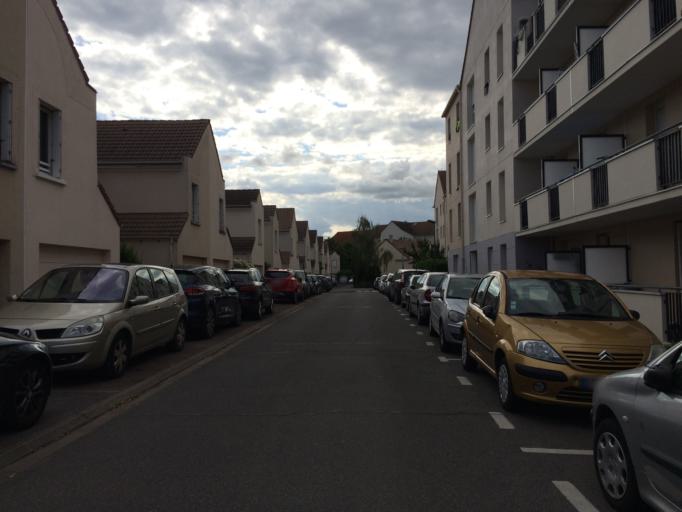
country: FR
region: Ile-de-France
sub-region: Departement de l'Essonne
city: Palaiseau
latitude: 48.7286
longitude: 2.2393
